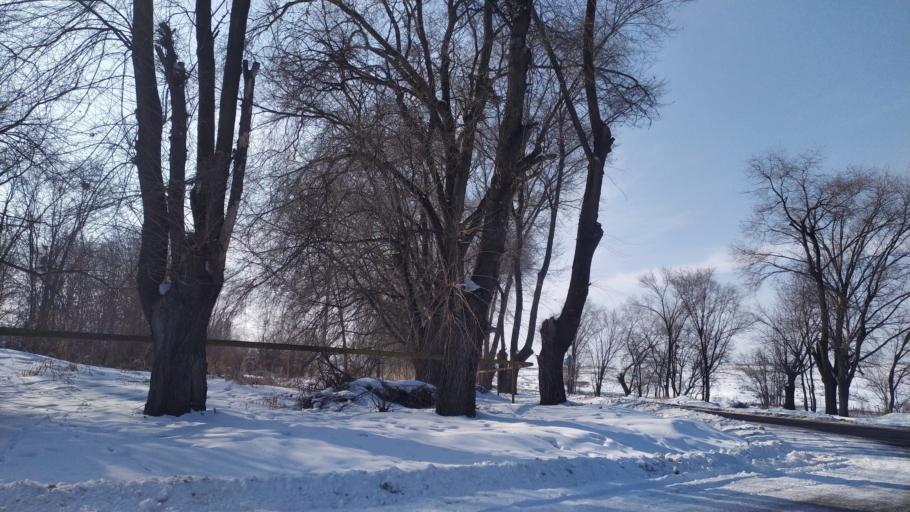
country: KZ
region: Almaty Oblysy
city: Burunday
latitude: 43.2340
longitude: 76.4066
